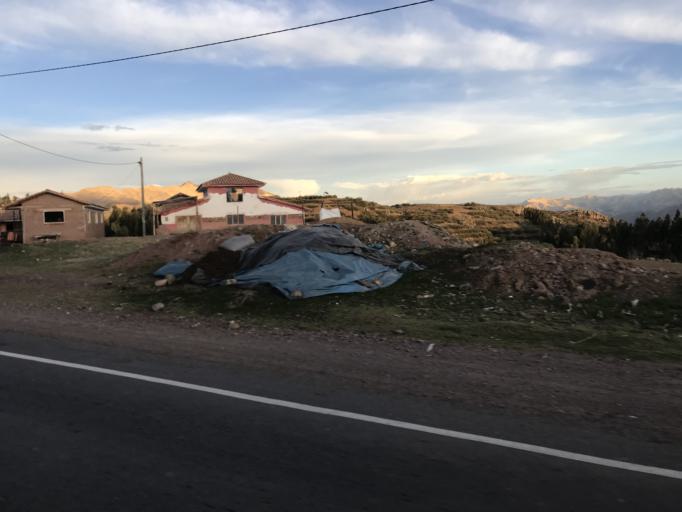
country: PE
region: Cusco
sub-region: Provincia de Cusco
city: Cusco
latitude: -13.4921
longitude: -71.9665
